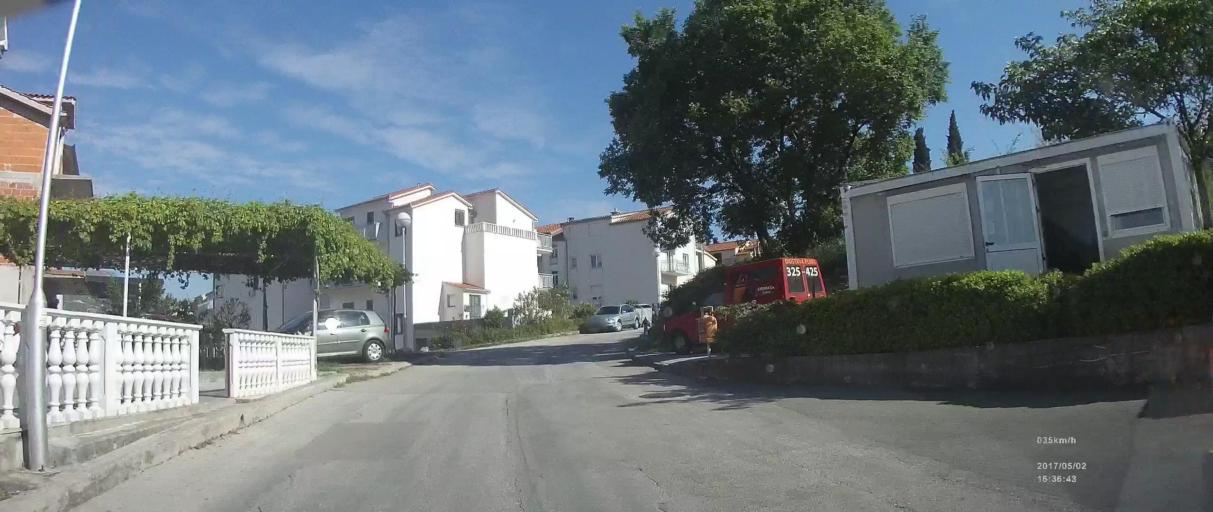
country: HR
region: Splitsko-Dalmatinska
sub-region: Grad Split
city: Stobrec
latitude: 43.5045
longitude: 16.5207
